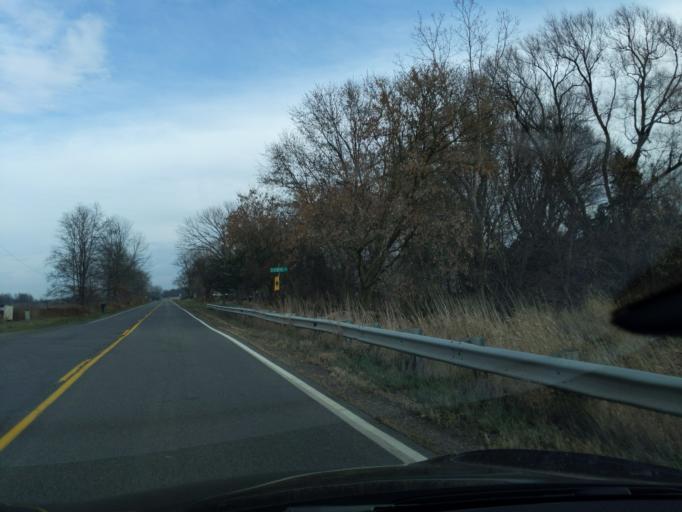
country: US
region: Michigan
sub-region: Ingham County
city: Mason
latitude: 42.6401
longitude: -84.4135
